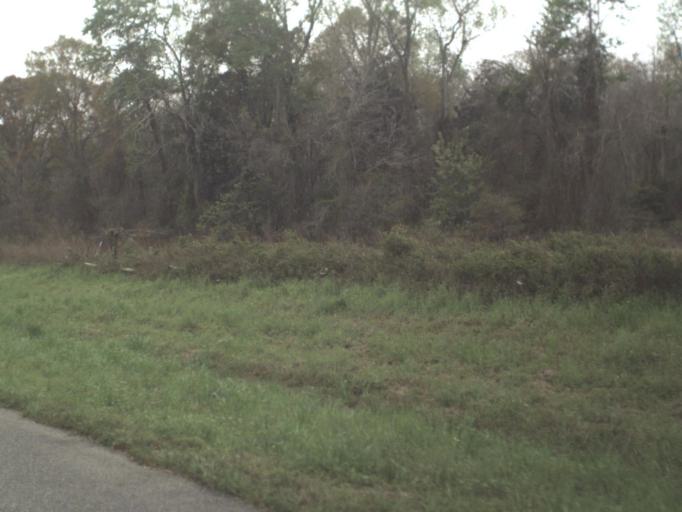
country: US
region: Florida
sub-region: Gadsden County
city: Gretna
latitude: 30.5418
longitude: -84.6771
